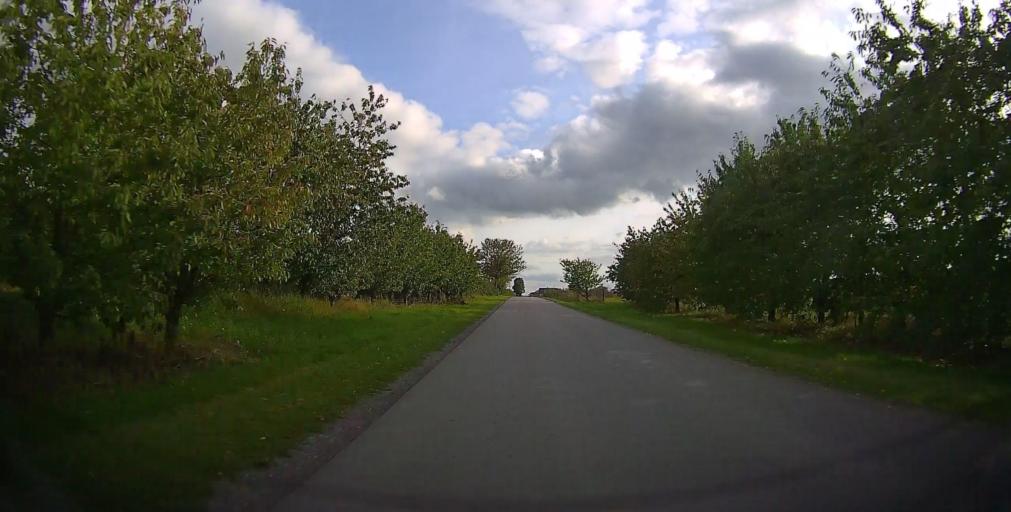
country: PL
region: Masovian Voivodeship
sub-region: Powiat bialobrzeski
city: Promna
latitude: 51.7449
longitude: 20.9644
